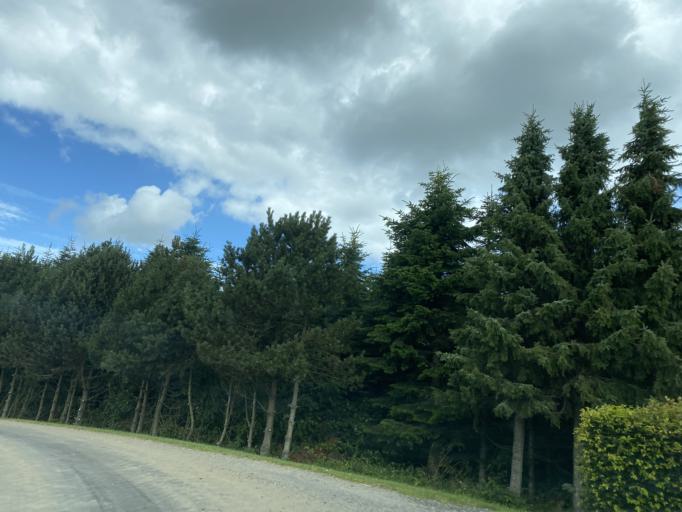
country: DK
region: Central Jutland
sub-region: Silkeborg Kommune
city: Svejbaek
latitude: 56.2388
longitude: 9.6375
